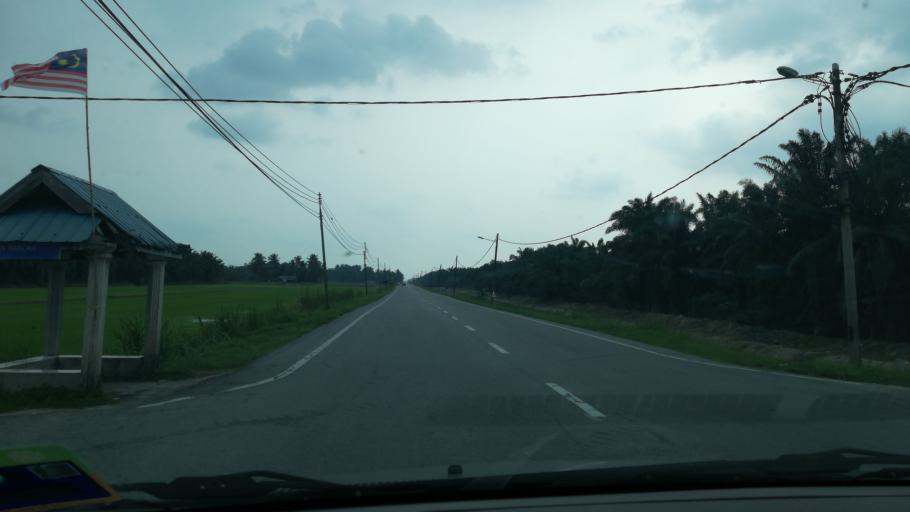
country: MY
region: Perak
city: Teluk Intan
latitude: 4.1195
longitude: 101.0780
